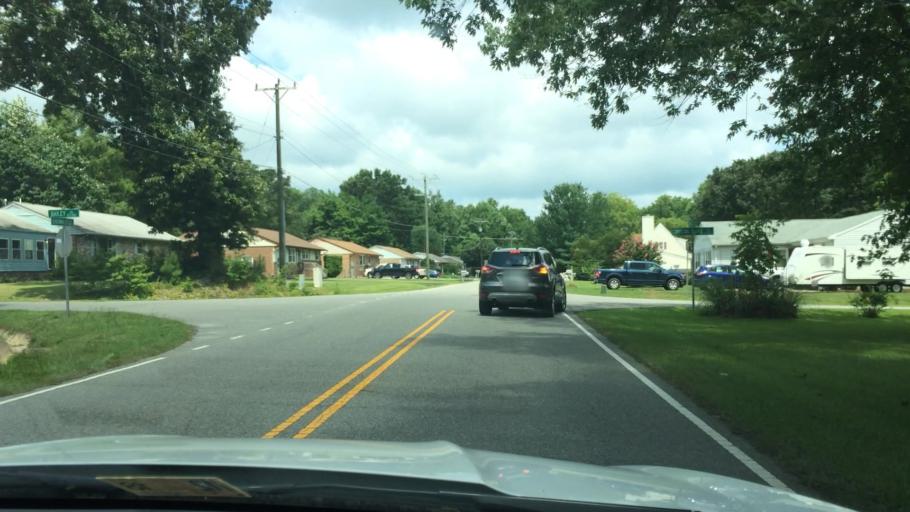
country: US
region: Virginia
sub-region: City of Poquoson
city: Poquoson
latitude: 37.1493
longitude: -76.4494
